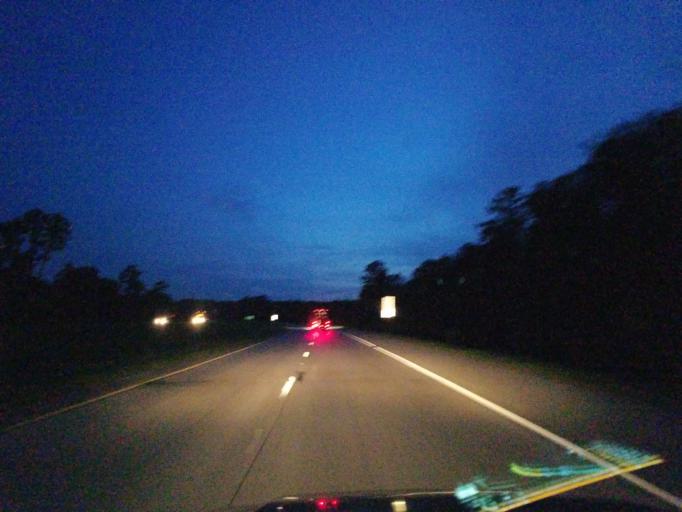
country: US
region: Mississippi
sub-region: Forrest County
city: Rawls Springs
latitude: 31.4934
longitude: -89.3193
